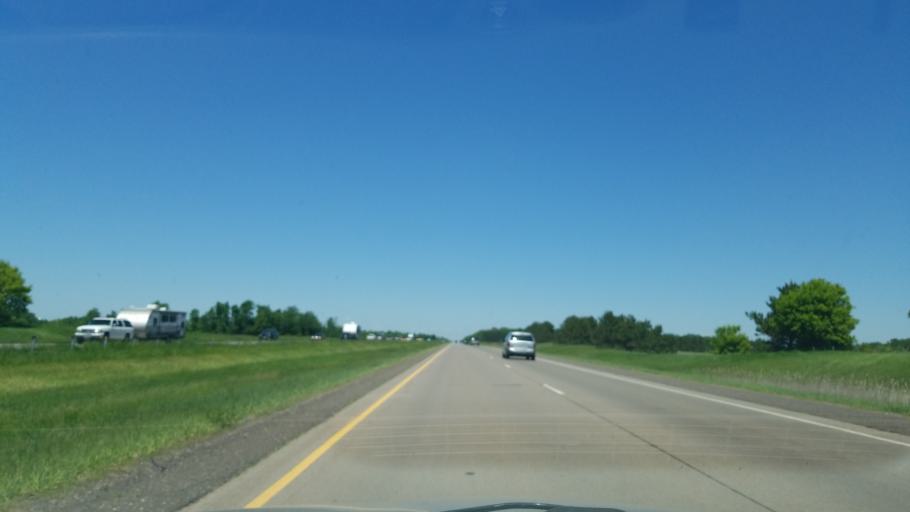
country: US
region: Minnesota
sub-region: Chisago County
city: Harris
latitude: 45.6181
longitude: -92.9921
